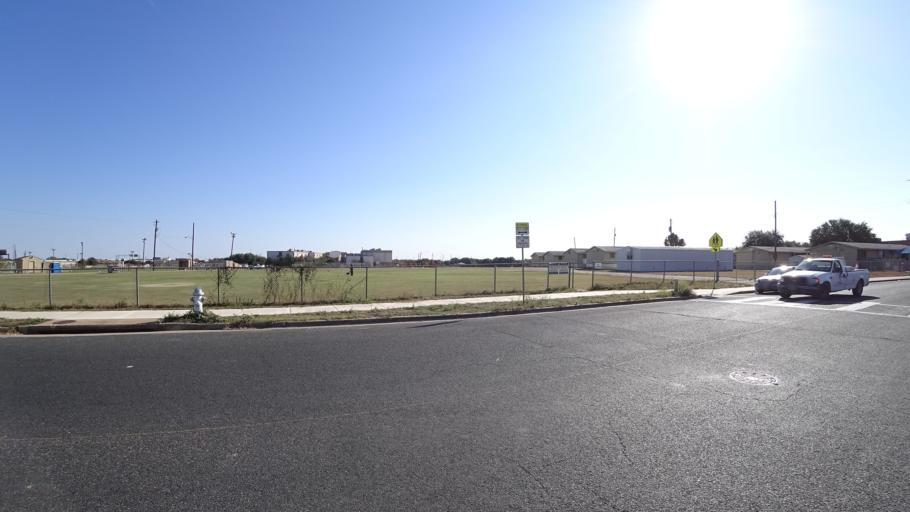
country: US
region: Texas
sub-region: Travis County
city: Barton Creek
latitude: 30.2339
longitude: -97.8457
